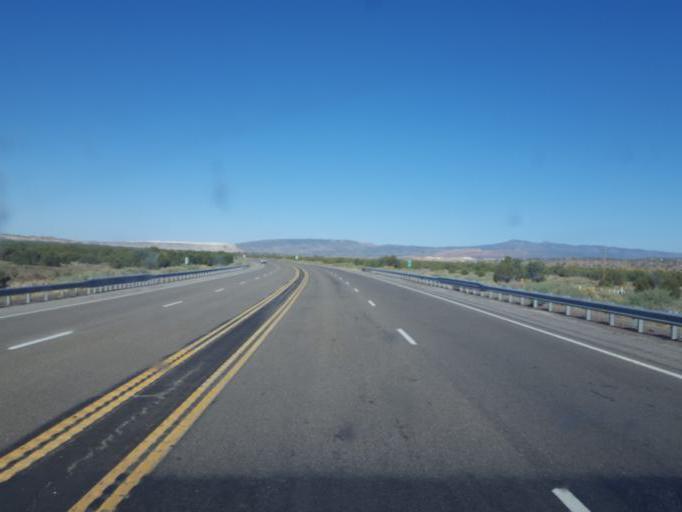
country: US
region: New Mexico
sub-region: Sandoval County
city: Jemez Pueblo
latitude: 35.4822
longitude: -106.7011
